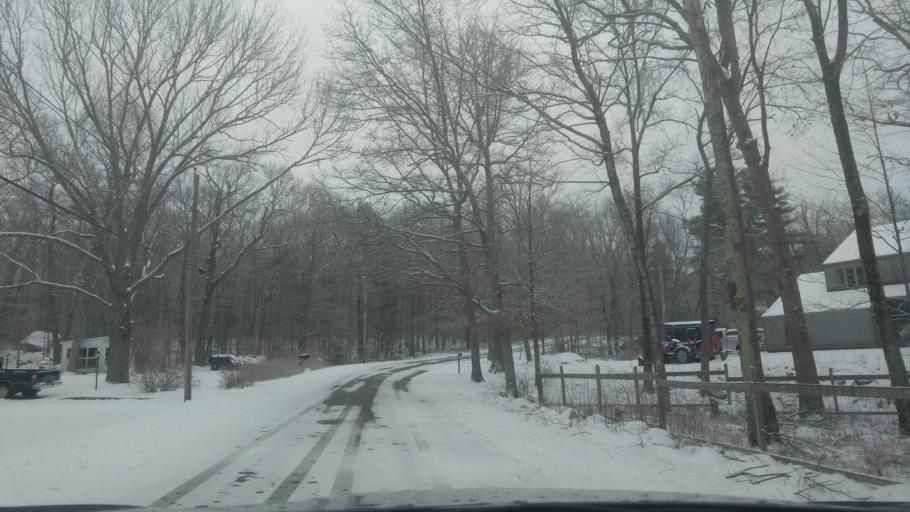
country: US
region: Rhode Island
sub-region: Providence County
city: Foster
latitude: 41.8276
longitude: -71.7442
